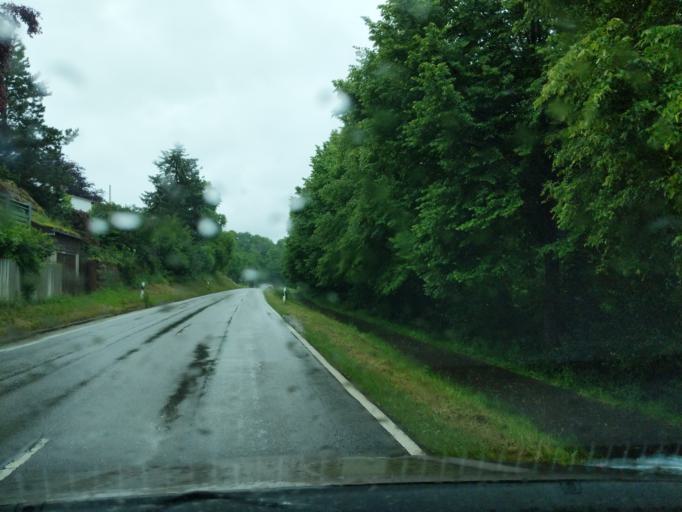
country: DE
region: Bavaria
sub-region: Upper Palatinate
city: Pettendorf
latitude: 49.0363
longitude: 12.0292
